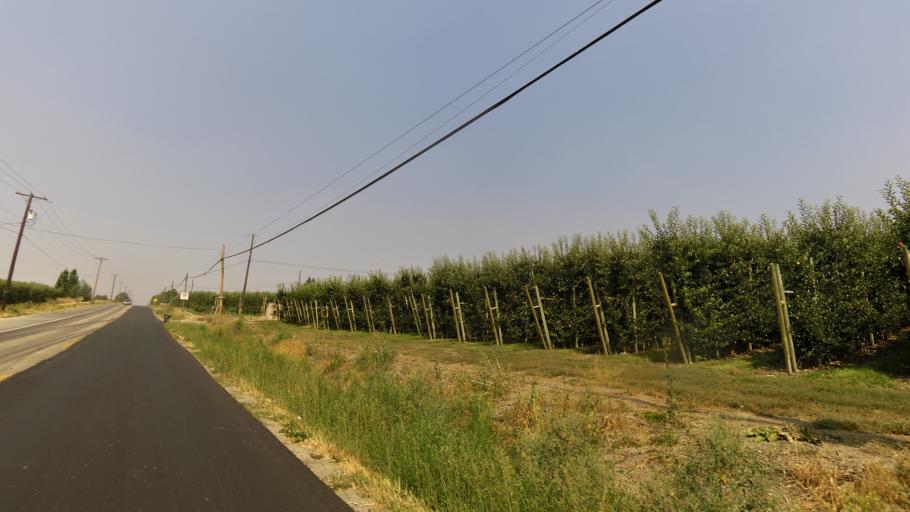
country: CA
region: British Columbia
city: Kelowna
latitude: 49.9276
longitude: -119.3641
